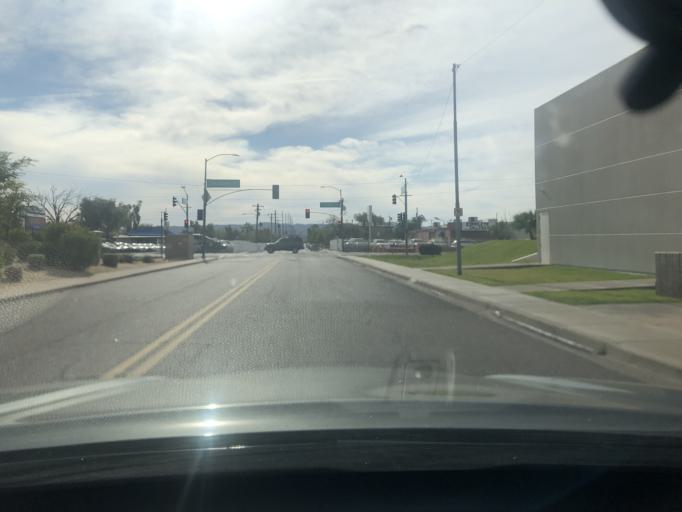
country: US
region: Arizona
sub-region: Maricopa County
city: Phoenix
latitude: 33.4521
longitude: -112.0434
